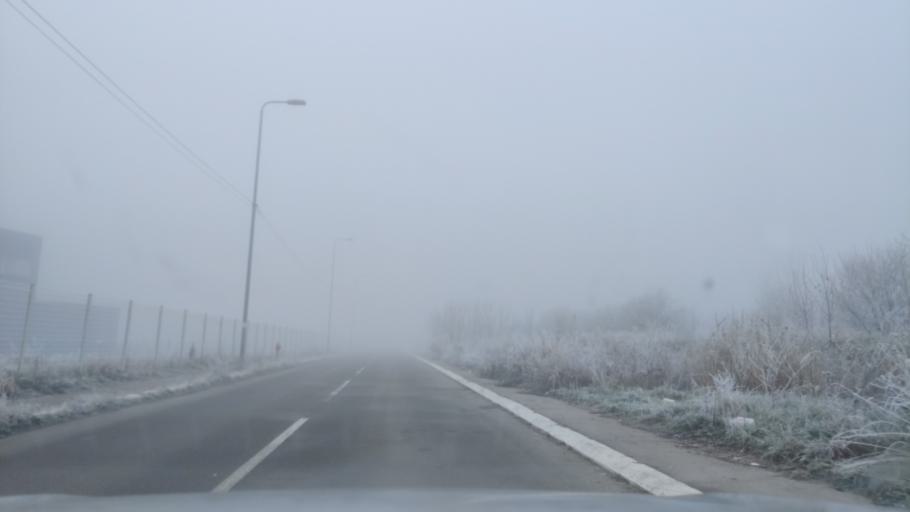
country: RS
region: Central Serbia
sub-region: Belgrade
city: Zemun
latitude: 44.8664
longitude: 20.3506
